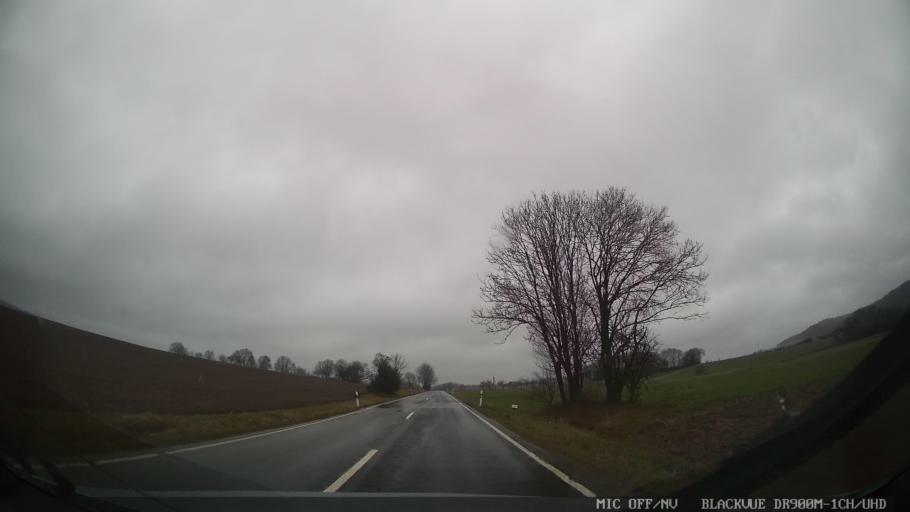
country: DE
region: Rheinland-Pfalz
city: Meckenbach
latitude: 49.6297
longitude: 7.1031
